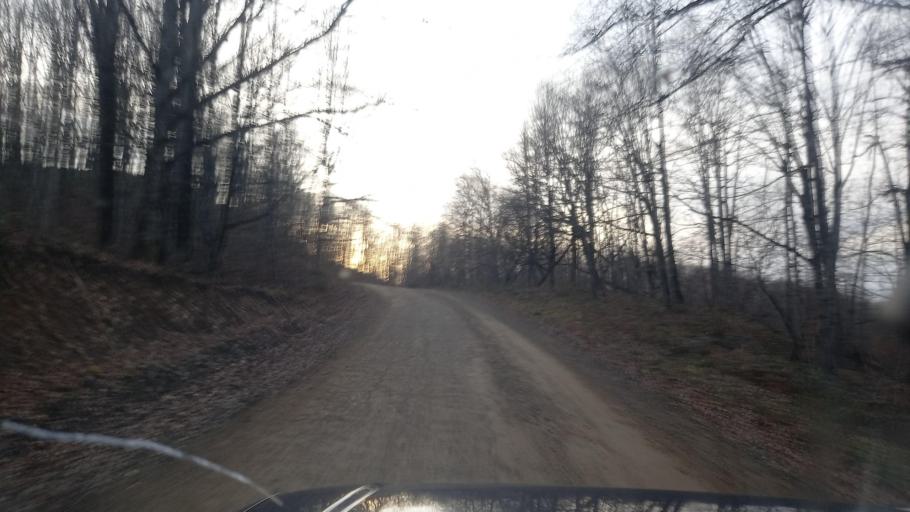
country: RU
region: Krasnodarskiy
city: Goryachiy Klyuch
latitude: 44.3707
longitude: 39.2142
